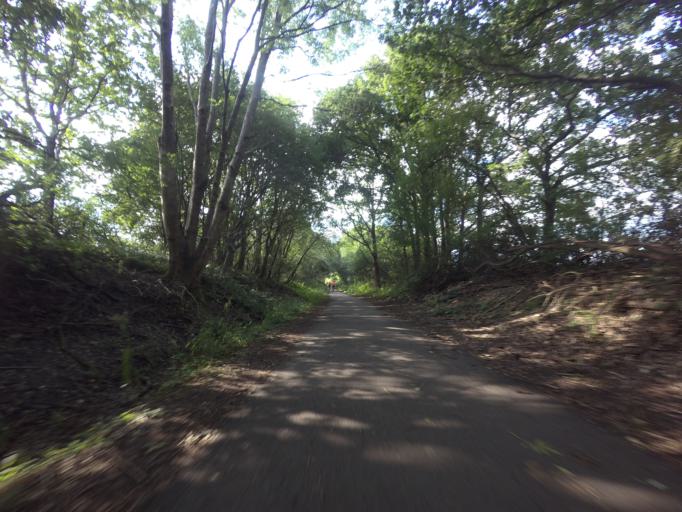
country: GB
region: England
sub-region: East Sussex
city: Horam
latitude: 50.9156
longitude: 0.2581
